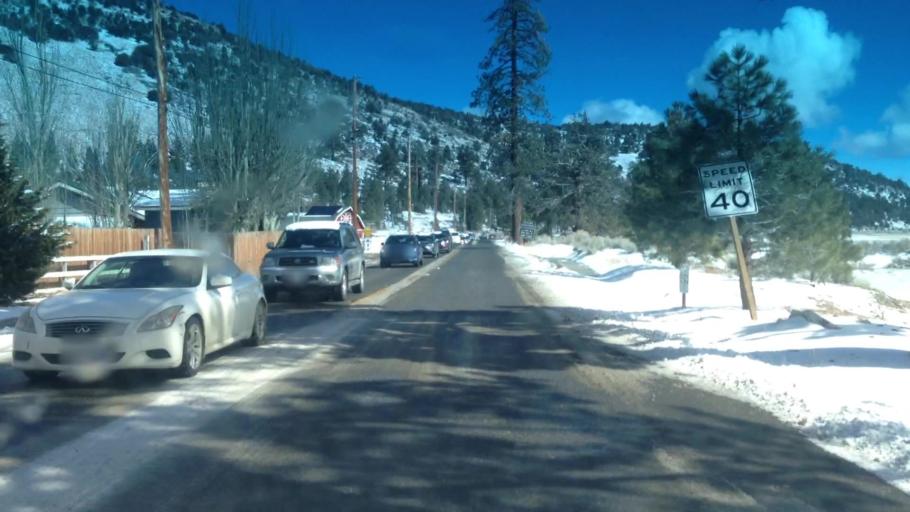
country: US
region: California
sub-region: San Bernardino County
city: Big Bear City
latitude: 34.2728
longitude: -116.8394
